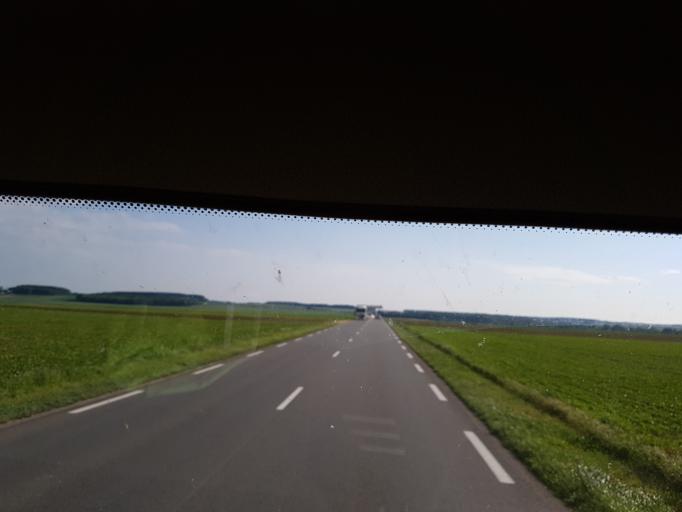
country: FR
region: Picardie
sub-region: Departement de la Somme
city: Crecy-en-Ponthieu
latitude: 50.2399
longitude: 1.9493
